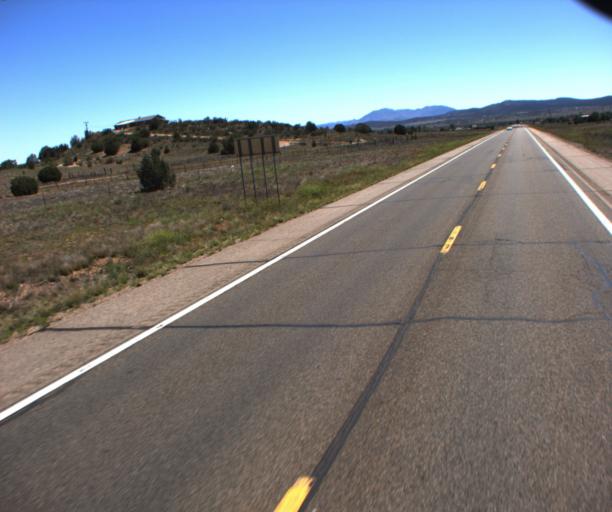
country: US
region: Arizona
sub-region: Yavapai County
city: Paulden
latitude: 34.9163
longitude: -112.4566
